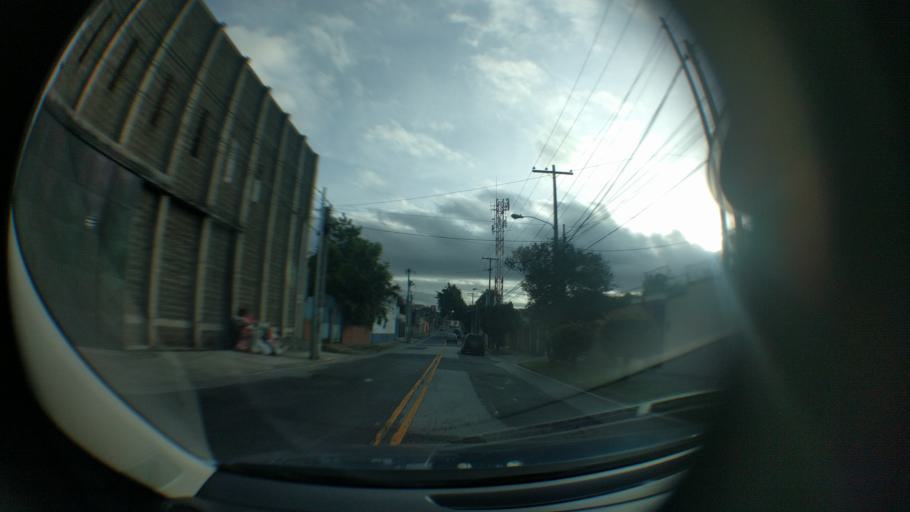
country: GT
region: Guatemala
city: Mixco
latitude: 14.5918
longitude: -90.5582
